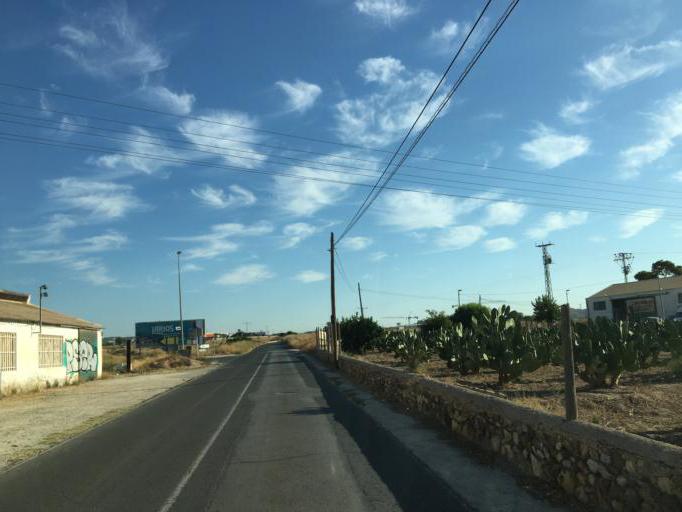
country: ES
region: Murcia
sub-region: Murcia
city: Murcia
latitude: 38.0319
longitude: -1.1208
